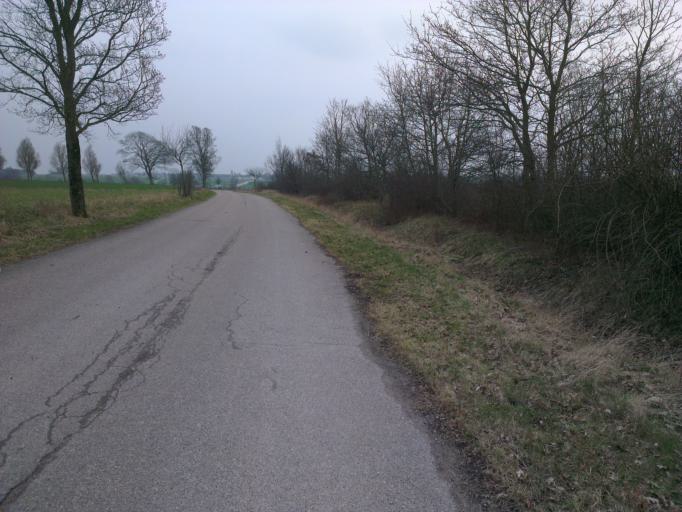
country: DK
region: Capital Region
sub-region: Frederikssund Kommune
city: Frederikssund
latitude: 55.8144
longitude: 12.1048
